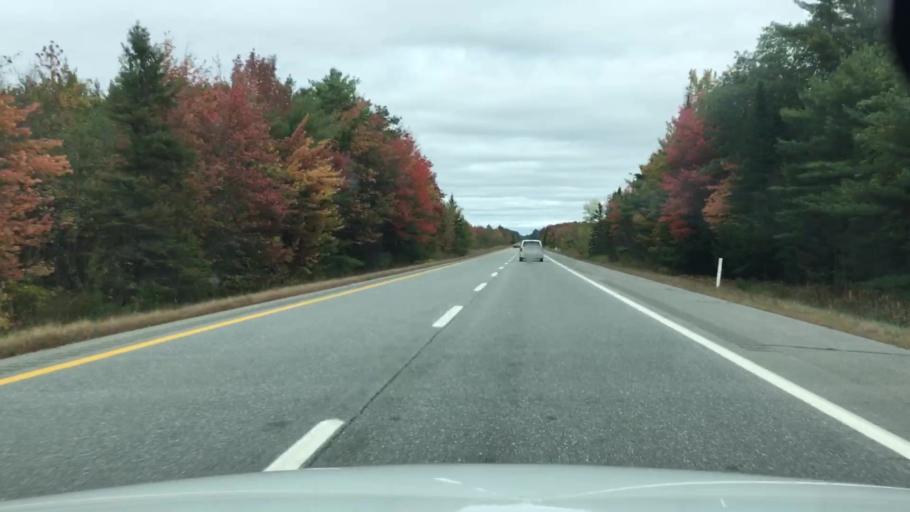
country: US
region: Maine
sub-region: Kennebec County
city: Benton
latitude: 44.6090
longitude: -69.5702
